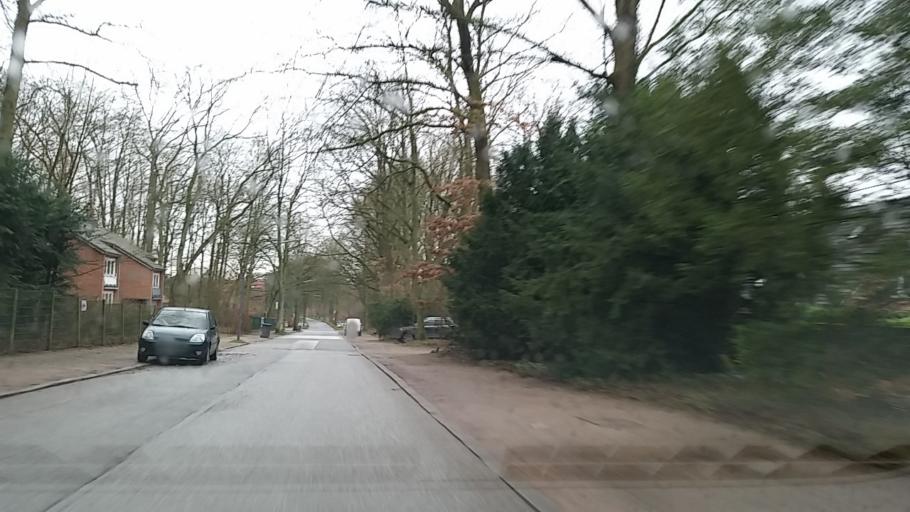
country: DE
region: Hamburg
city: Bergedorf
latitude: 53.4817
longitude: 10.2415
